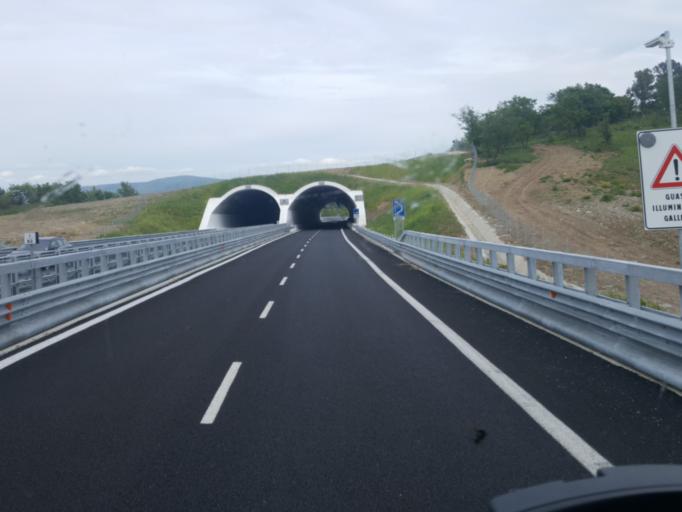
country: IT
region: Latium
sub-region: Provincia di Viterbo
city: Monte Romano
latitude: 42.2970
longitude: 11.9539
